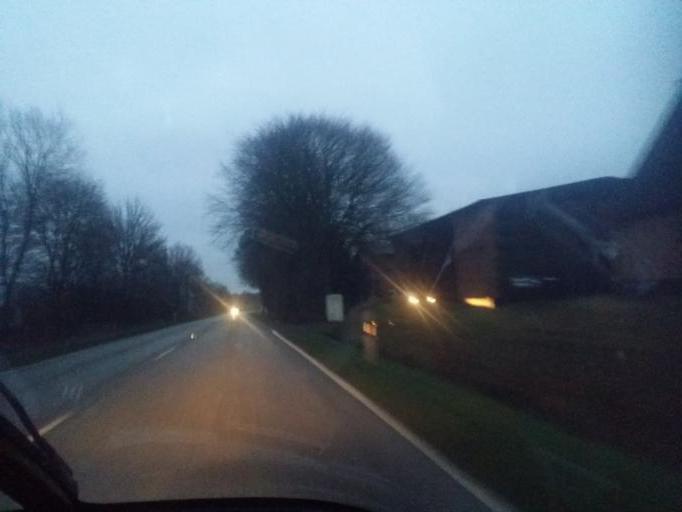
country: DE
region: Schleswig-Holstein
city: Warringholz
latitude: 54.0715
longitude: 9.4679
